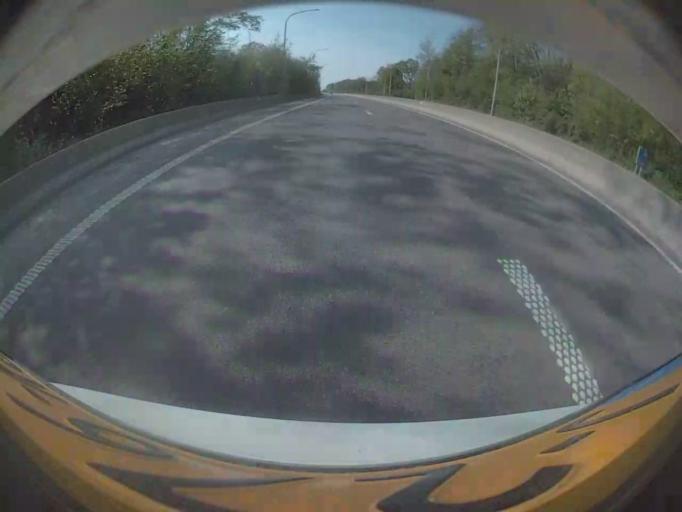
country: BE
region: Wallonia
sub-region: Province de Namur
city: Hamois
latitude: 50.3082
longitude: 5.1545
